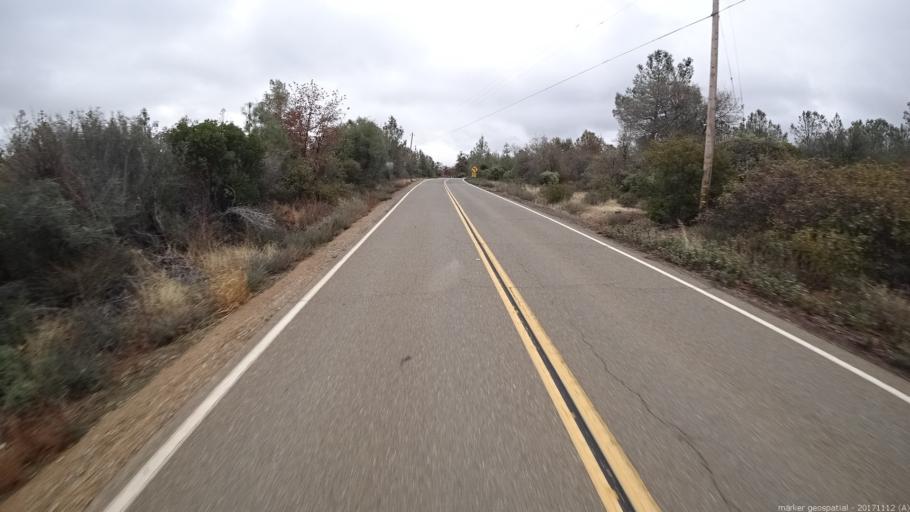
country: US
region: California
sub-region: Shasta County
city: Shingletown
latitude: 40.5123
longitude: -122.0329
